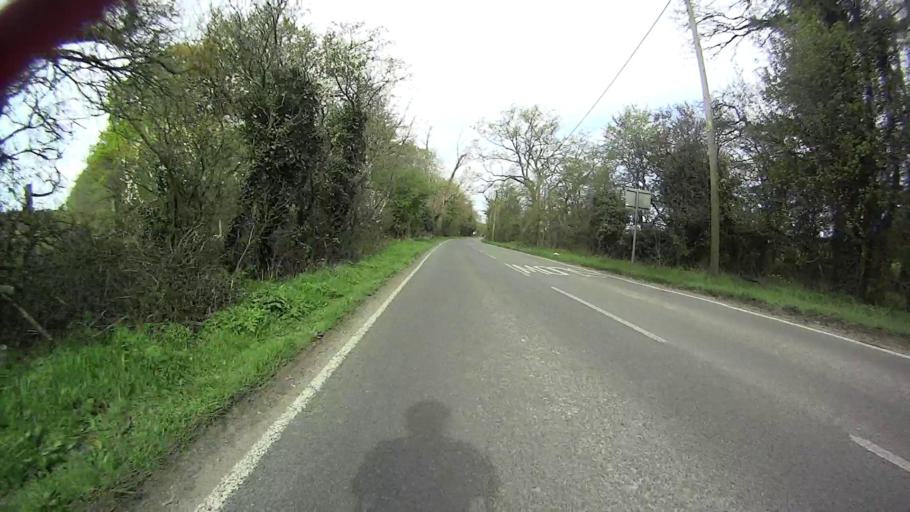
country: GB
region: England
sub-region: West Sussex
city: Langley Green
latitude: 51.1344
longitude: -0.2175
